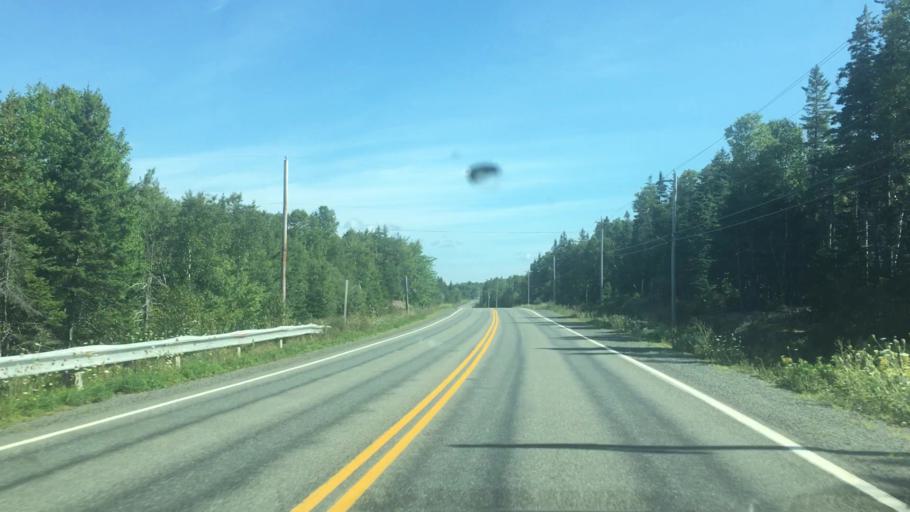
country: CA
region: Nova Scotia
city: Sydney
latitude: 45.9896
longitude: -60.4139
